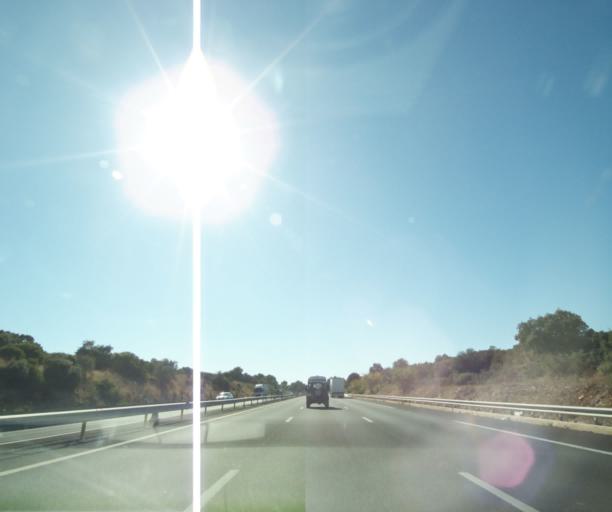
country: FR
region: Languedoc-Roussillon
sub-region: Departement de l'Herault
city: Fabregues
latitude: 43.5312
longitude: 3.7750
